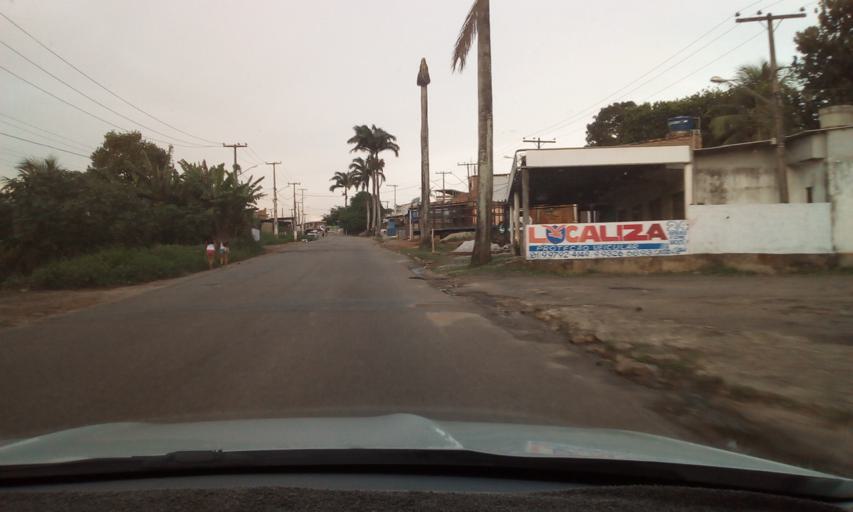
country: BR
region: Pernambuco
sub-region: Vicencia
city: Vicencia
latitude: -7.5989
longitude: -35.2331
